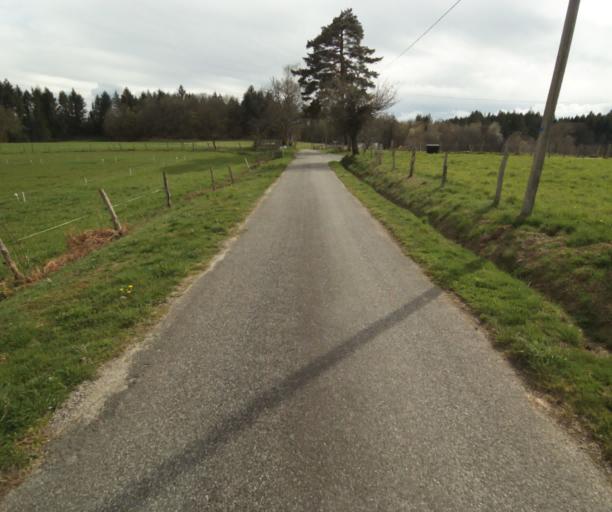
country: FR
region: Limousin
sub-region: Departement de la Correze
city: Argentat
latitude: 45.2117
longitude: 1.9587
